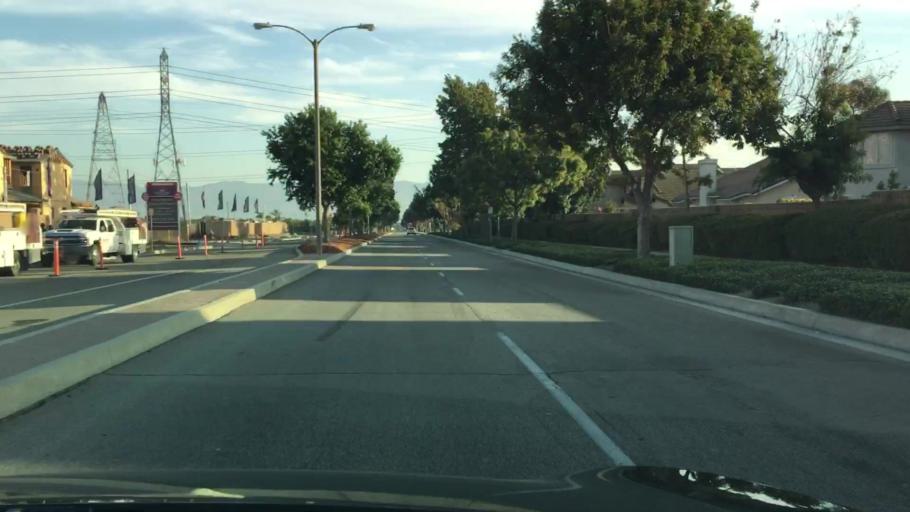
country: US
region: California
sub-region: San Bernardino County
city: Chino
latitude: 34.0028
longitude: -117.6544
